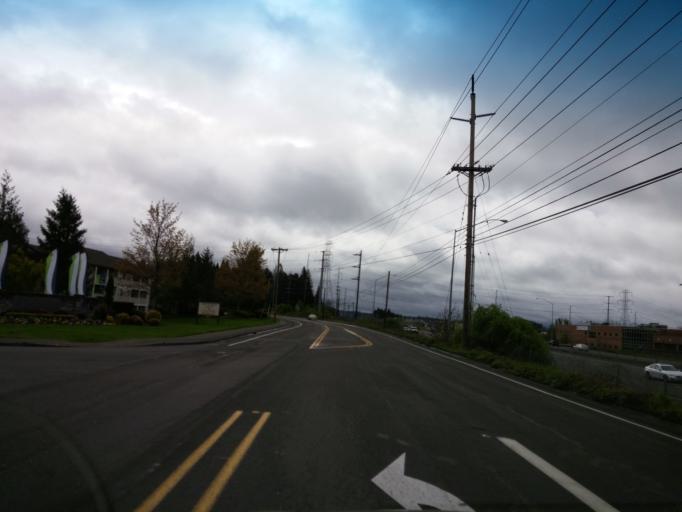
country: US
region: Oregon
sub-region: Washington County
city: Oak Hills
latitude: 45.5355
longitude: -122.8495
